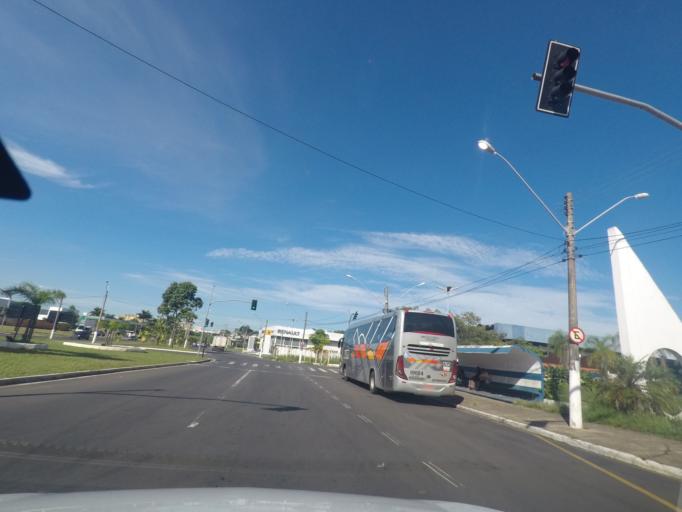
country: BR
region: Sao Paulo
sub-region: Rio Claro
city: Rio Claro
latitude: -22.4172
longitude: -47.5750
